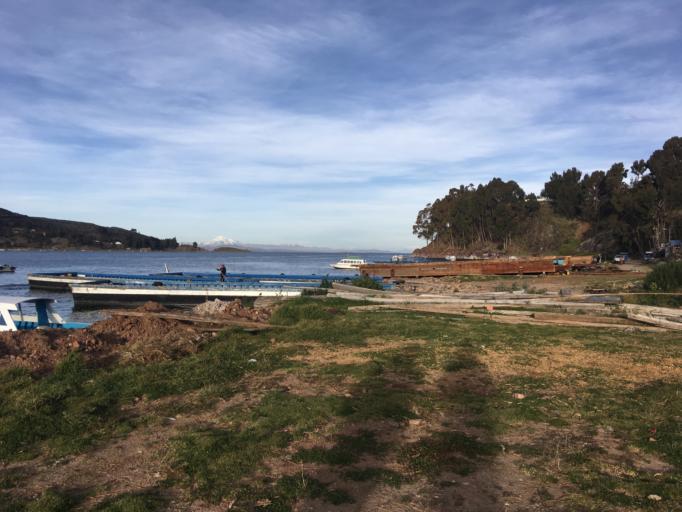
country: BO
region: La Paz
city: San Pedro
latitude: -16.2231
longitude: -68.8515
